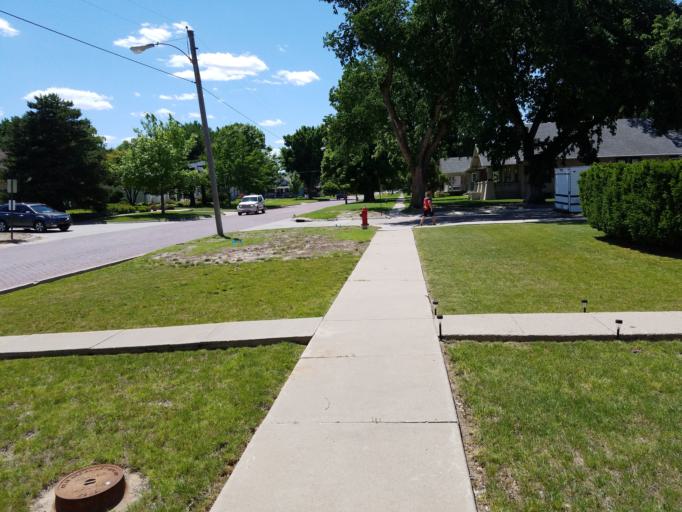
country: US
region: Kansas
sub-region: Decatur County
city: Oberlin
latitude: 39.8209
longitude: -100.5239
